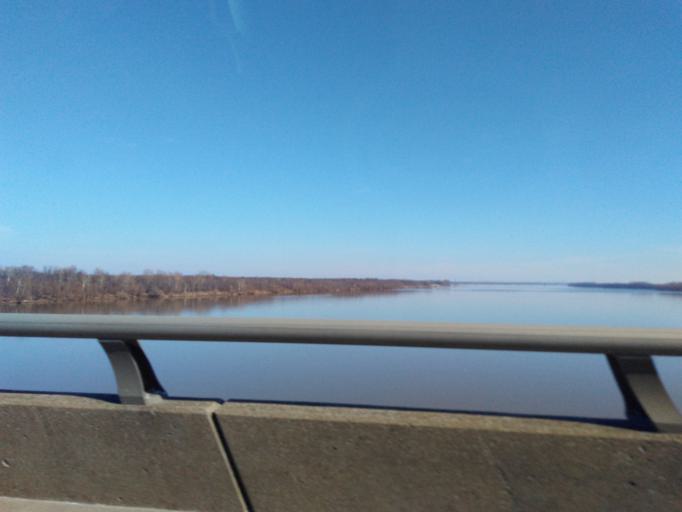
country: US
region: Illinois
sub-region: Massac County
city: Metropolis
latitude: 37.1350
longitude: -88.6865
